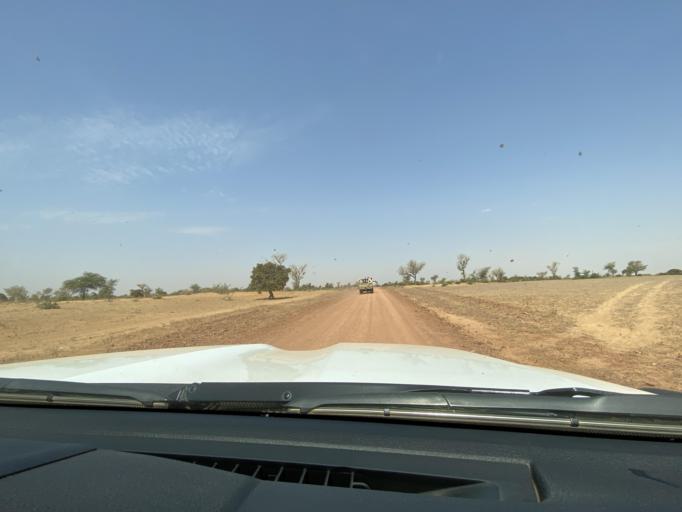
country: NE
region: Dosso
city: Birnin Gaoure
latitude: 13.2335
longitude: 2.8686
